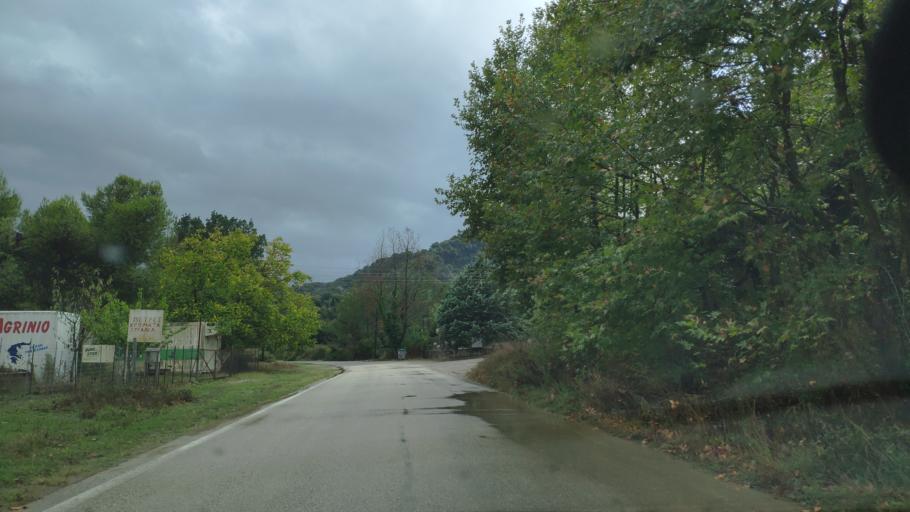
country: GR
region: West Greece
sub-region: Nomos Aitolias kai Akarnanias
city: Krikellos
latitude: 38.9642
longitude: 21.3286
